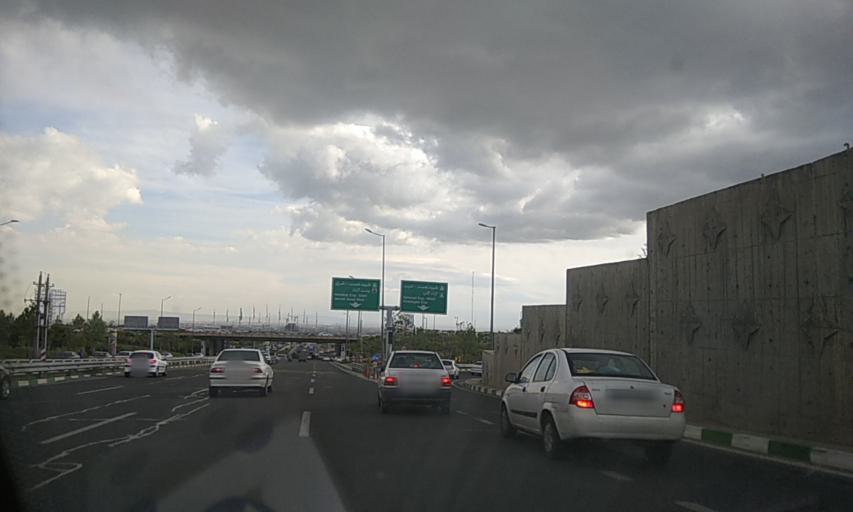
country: IR
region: Tehran
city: Tajrish
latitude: 35.7557
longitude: 51.2951
